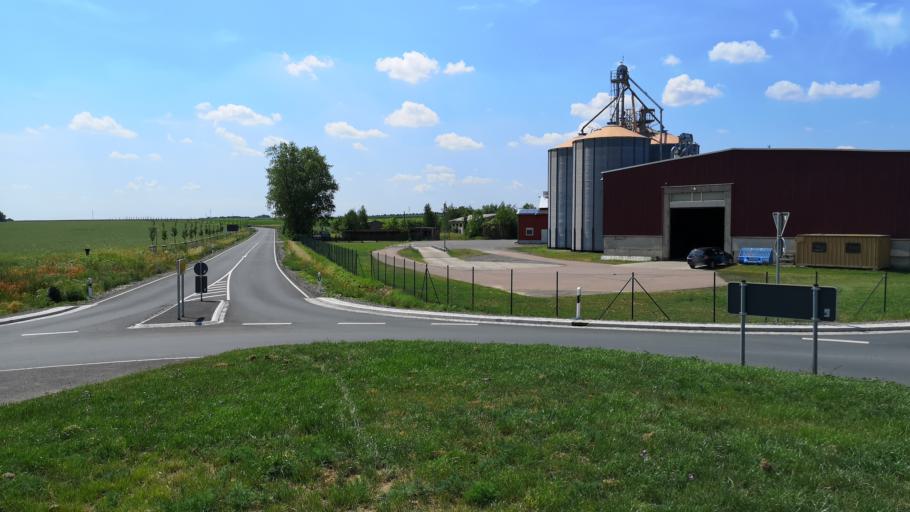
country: DE
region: Saxony-Anhalt
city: Mansfeld
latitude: 51.6539
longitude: 11.4300
